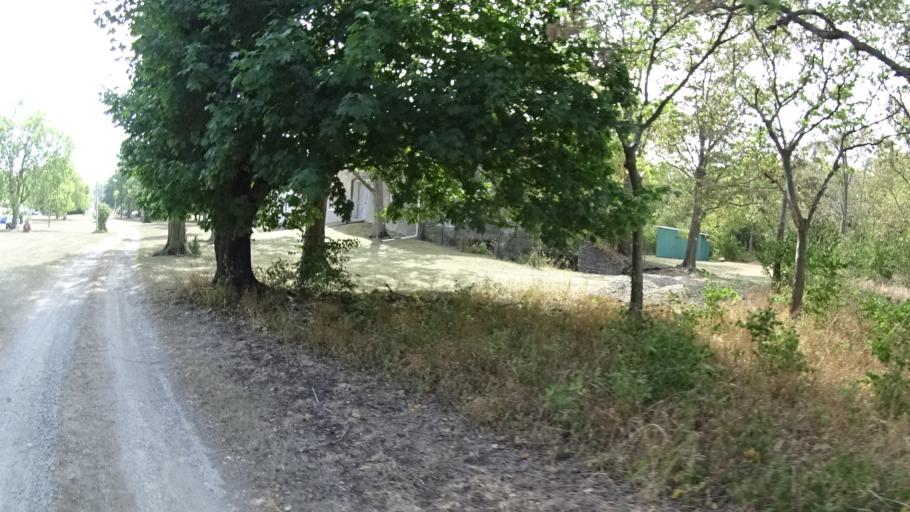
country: US
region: Ohio
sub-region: Erie County
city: Sandusky
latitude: 41.5980
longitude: -82.7021
